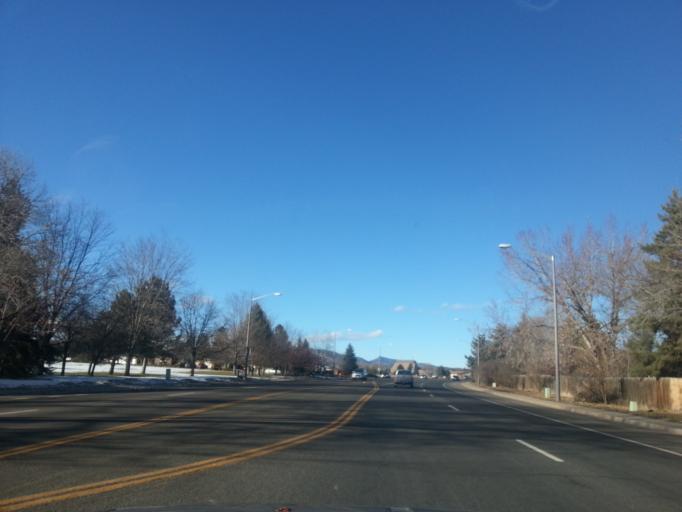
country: US
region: Colorado
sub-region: Larimer County
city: Loveland
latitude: 40.4183
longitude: -105.1144
